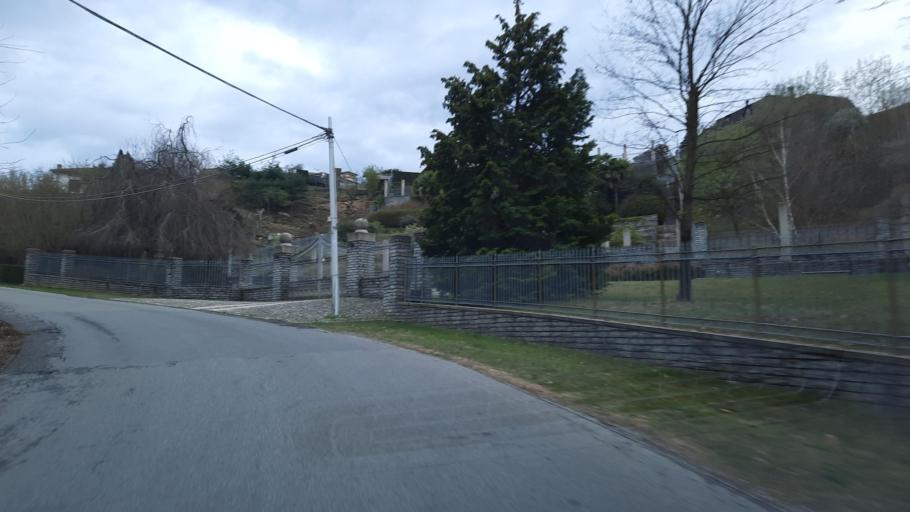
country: IT
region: Piedmont
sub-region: Provincia di Novara
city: San Maurizio D'Opaglio
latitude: 45.7789
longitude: 8.3927
